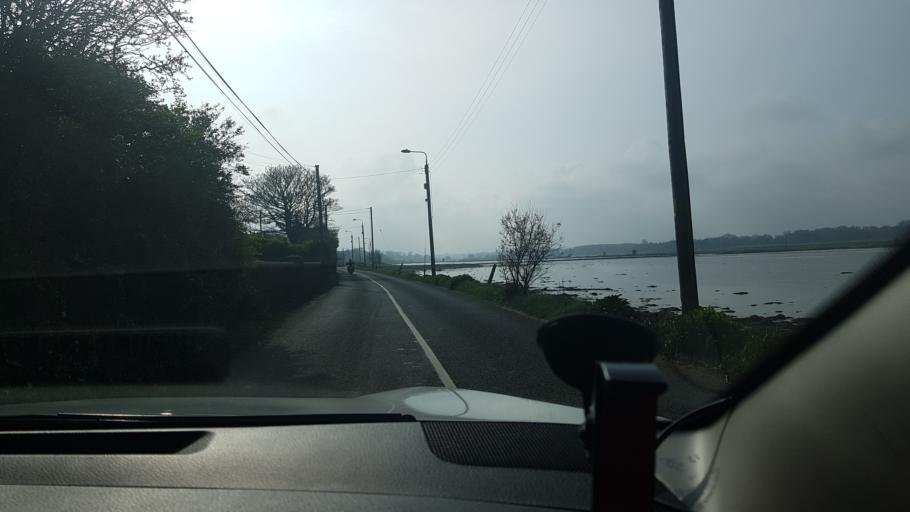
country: IE
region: Leinster
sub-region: Lu
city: Termonfeckin
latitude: 53.7231
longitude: -6.2776
